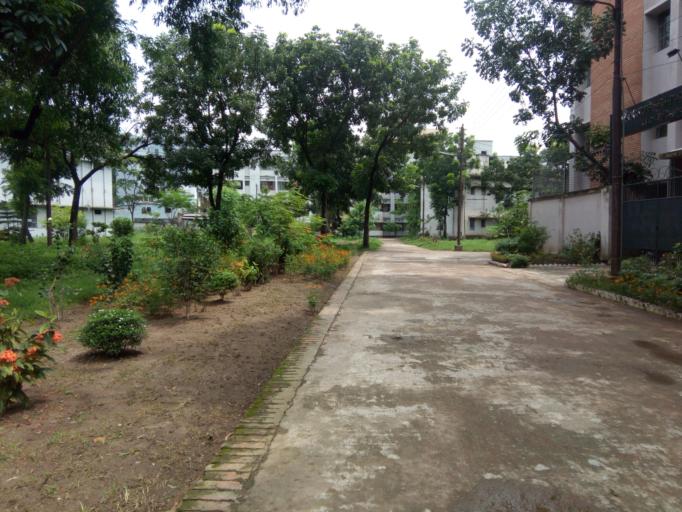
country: BD
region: Dhaka
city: Azimpur
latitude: 23.7316
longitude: 90.3700
